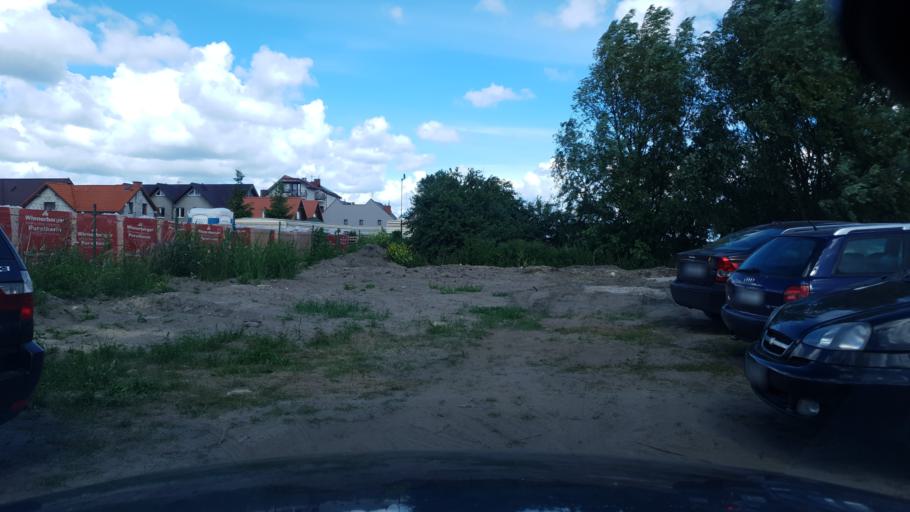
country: PL
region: Pomeranian Voivodeship
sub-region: Powiat pucki
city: Mosty
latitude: 54.6312
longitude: 18.5096
